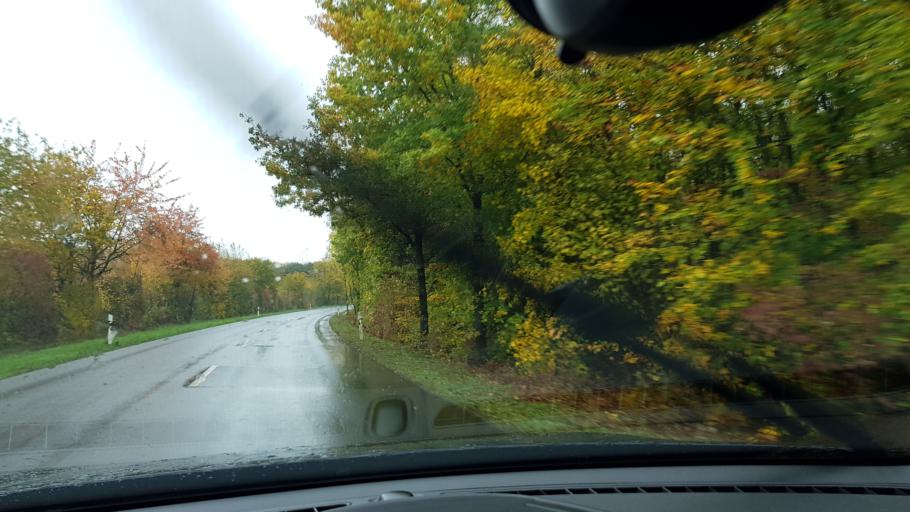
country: DE
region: North Rhine-Westphalia
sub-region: Regierungsbezirk Dusseldorf
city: Grevenbroich
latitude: 51.0453
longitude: 6.5875
